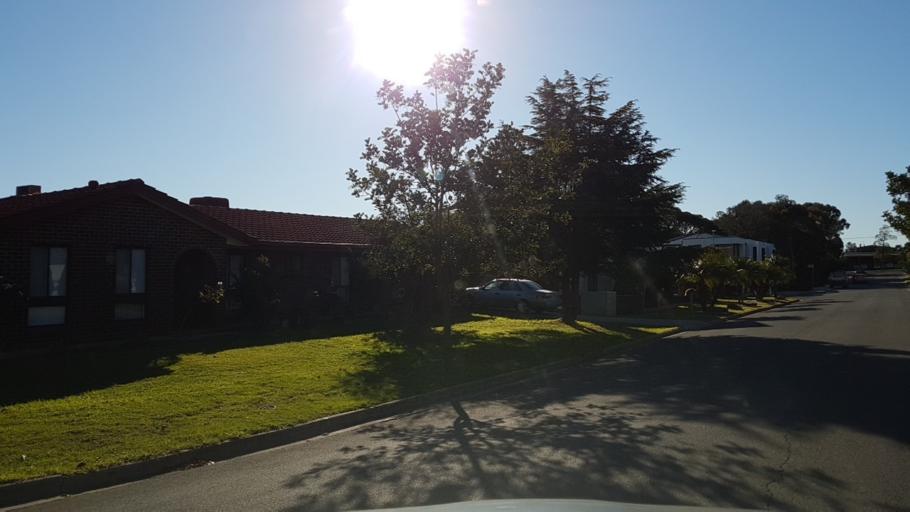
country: AU
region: South Australia
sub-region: Campbelltown
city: Campbelltown
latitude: -34.8828
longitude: 138.6843
